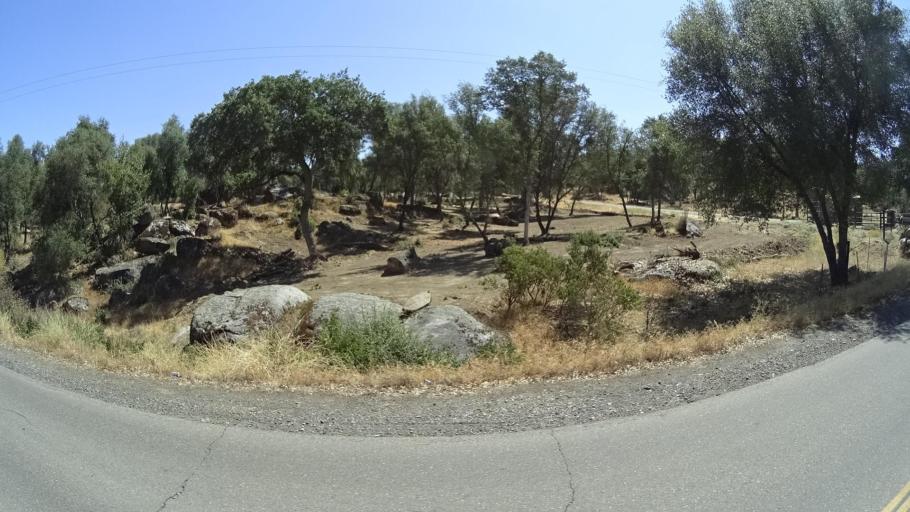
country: US
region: California
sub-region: Mariposa County
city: Mariposa
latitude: 37.4482
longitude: -119.9391
